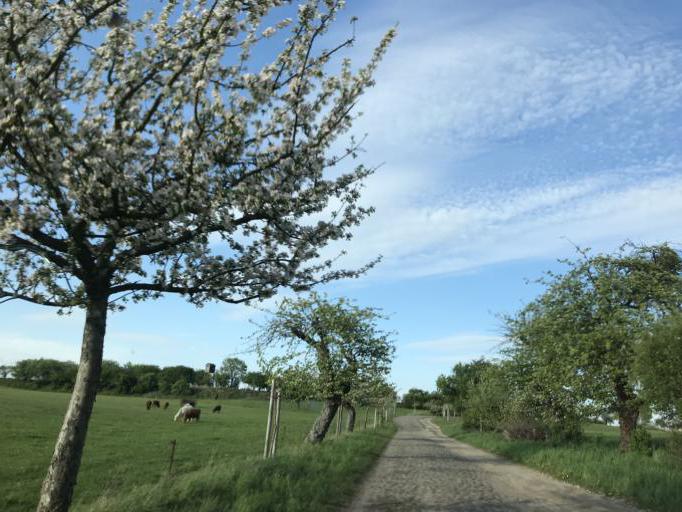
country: DE
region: Brandenburg
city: Joachimsthal
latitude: 52.9747
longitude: 13.7269
